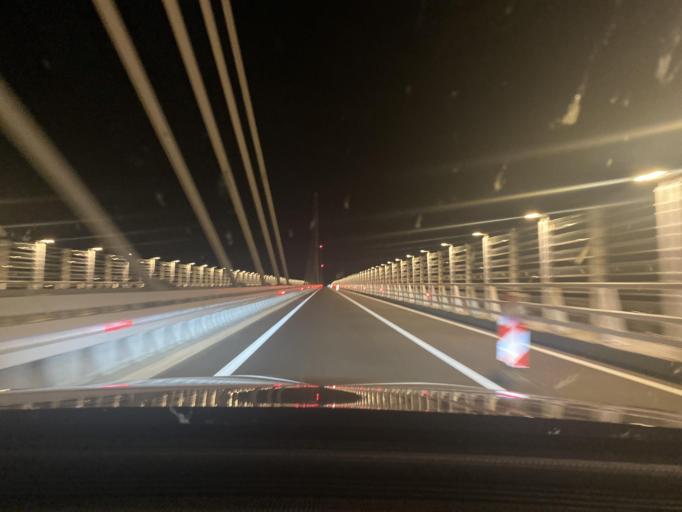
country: BA
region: Federation of Bosnia and Herzegovina
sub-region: Hercegovacko-Bosanski Kanton
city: Neum
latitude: 42.9367
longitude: 17.5408
